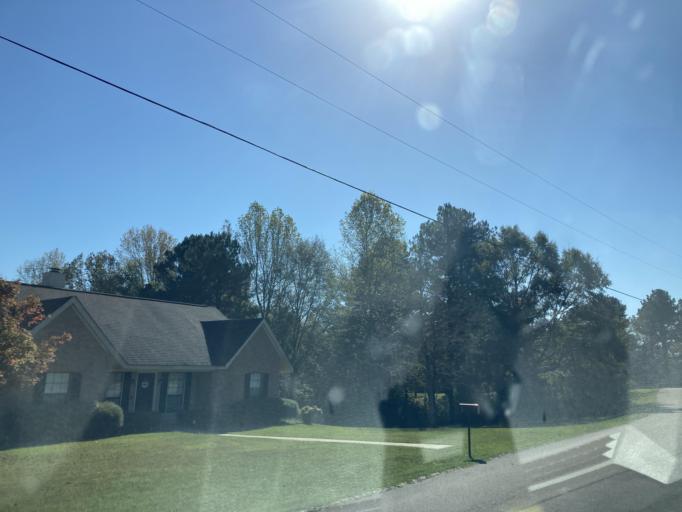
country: US
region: Mississippi
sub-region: Lamar County
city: West Hattiesburg
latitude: 31.2998
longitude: -89.4053
